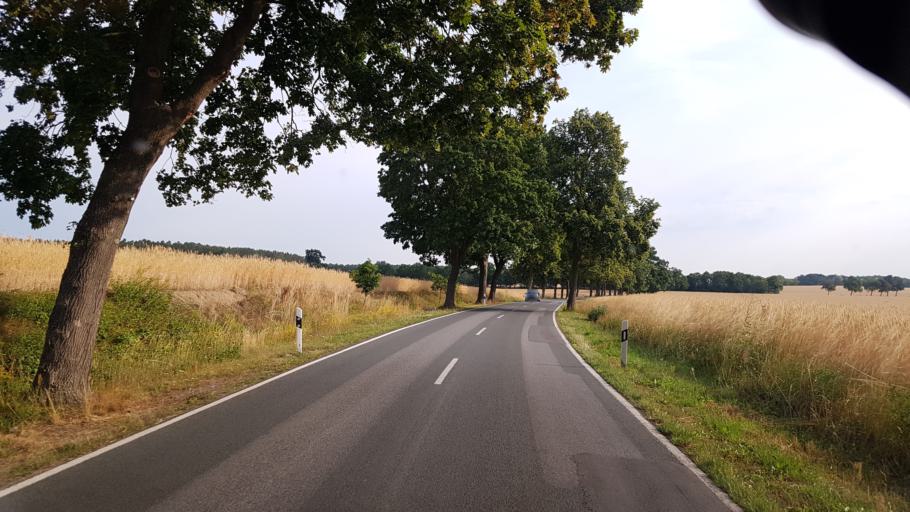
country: DE
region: Brandenburg
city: Golssen
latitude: 51.9614
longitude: 13.5429
